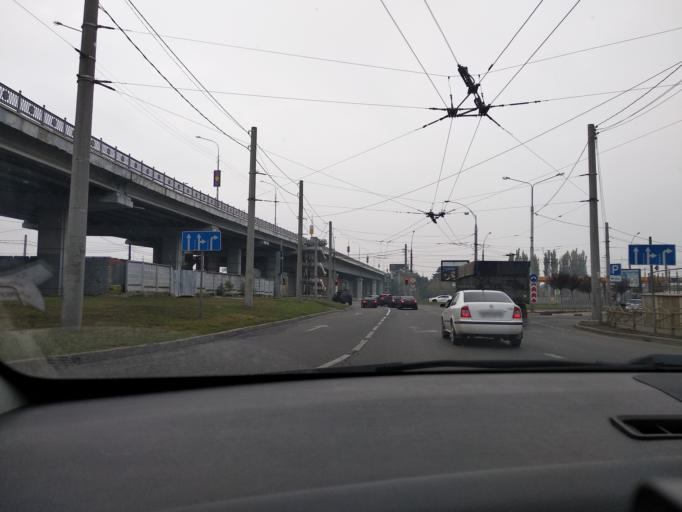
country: RU
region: Krasnodarskiy
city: Krasnodar
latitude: 45.0375
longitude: 38.9543
